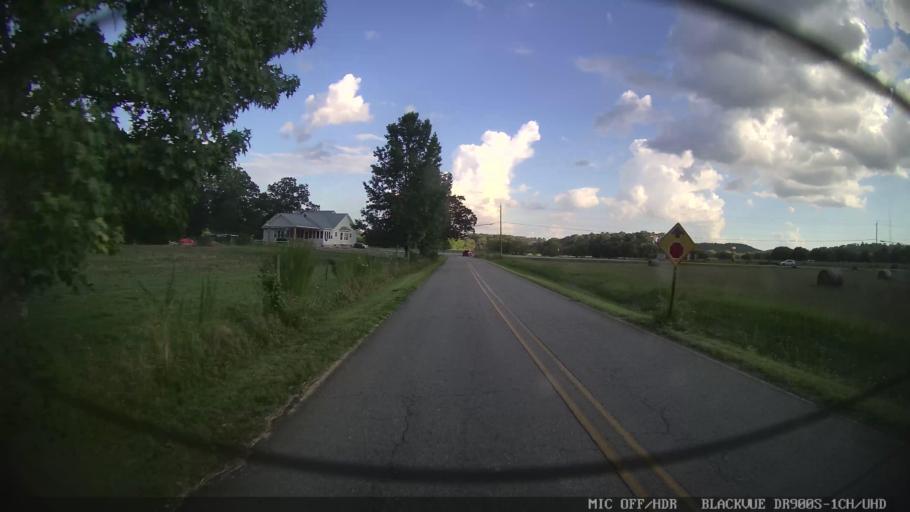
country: US
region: Georgia
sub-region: Bartow County
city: Rydal
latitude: 34.2725
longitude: -84.7980
